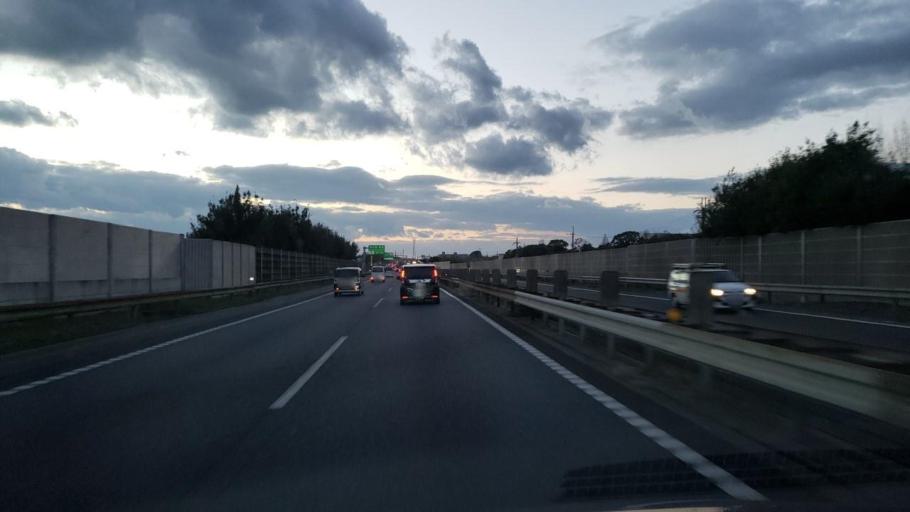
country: JP
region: Hyogo
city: Kakogawacho-honmachi
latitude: 34.7166
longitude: 134.9119
